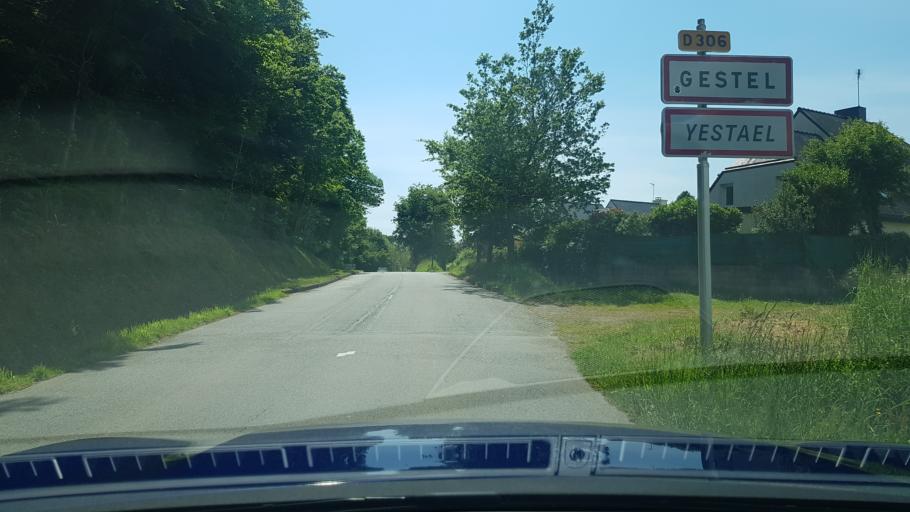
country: FR
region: Brittany
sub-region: Departement du Morbihan
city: Gestel
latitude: 47.8067
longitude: -3.4363
